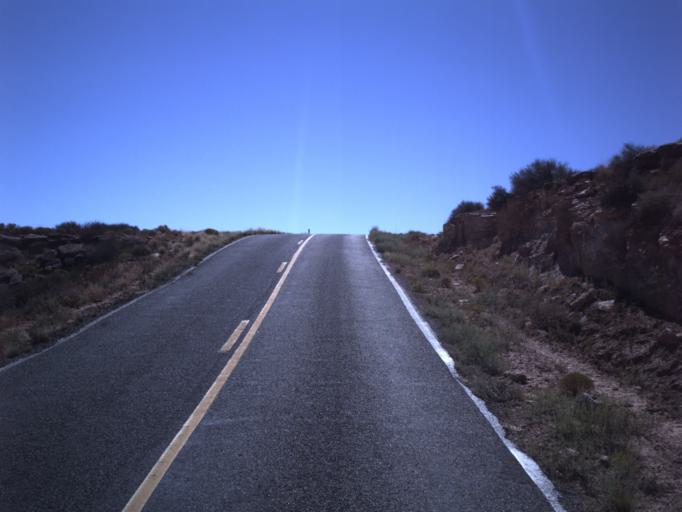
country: US
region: Arizona
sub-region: Navajo County
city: Kayenta
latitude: 37.1833
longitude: -109.9210
